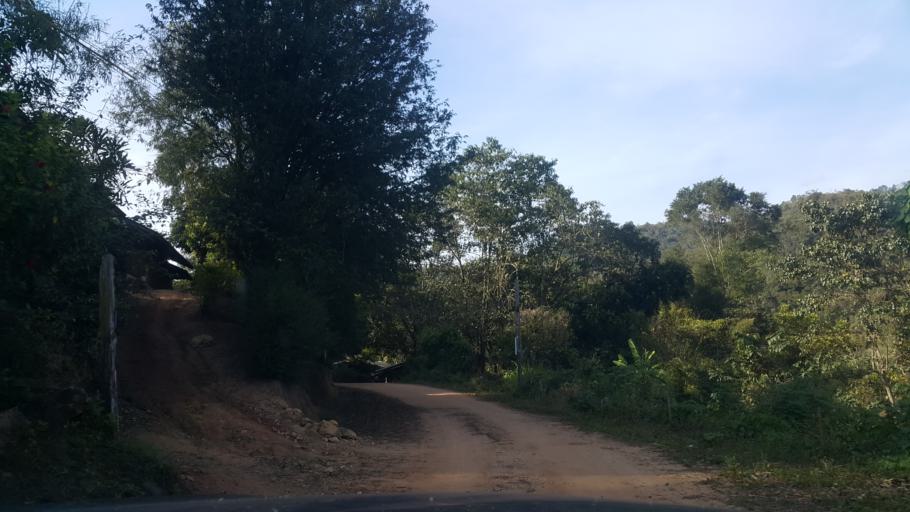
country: TH
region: Chiang Mai
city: Samoeng
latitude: 18.9599
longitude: 98.6725
